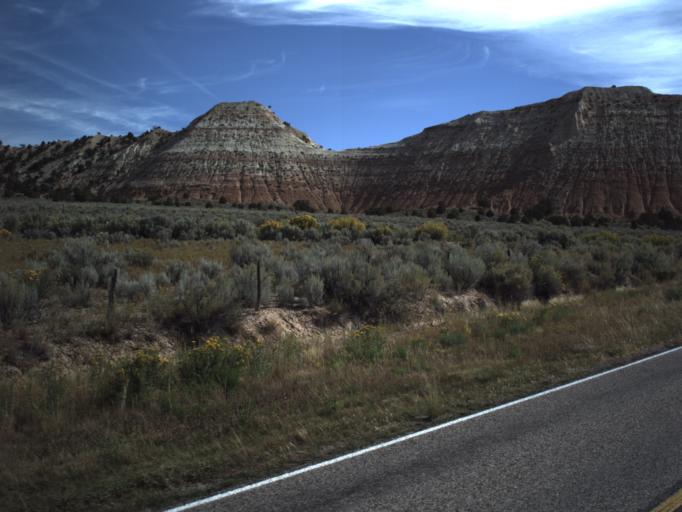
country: US
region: Utah
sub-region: Garfield County
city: Panguitch
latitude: 37.5649
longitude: -112.0440
